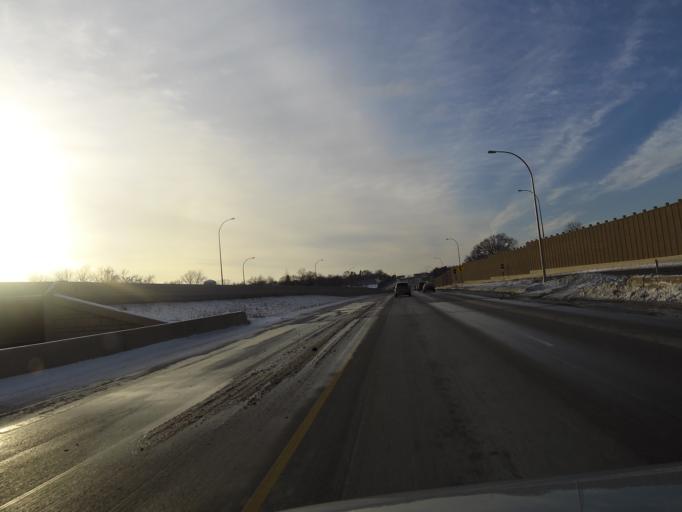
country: US
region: Minnesota
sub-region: Hennepin County
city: Richfield
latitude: 44.8904
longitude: -93.2957
